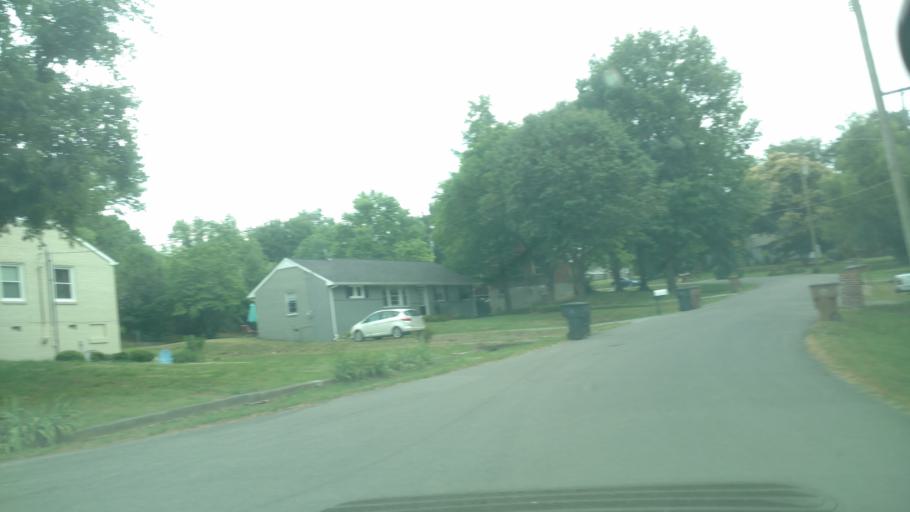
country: US
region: Tennessee
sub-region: Davidson County
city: Nashville
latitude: 36.1948
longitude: -86.7075
